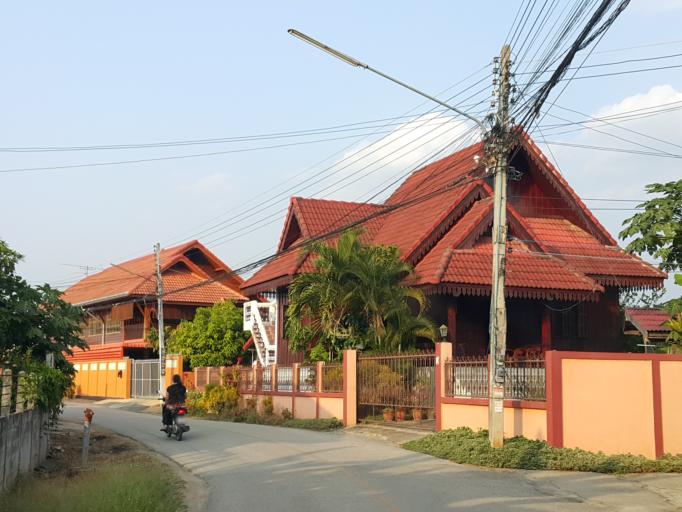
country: TH
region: Chiang Mai
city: San Sai
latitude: 18.8816
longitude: 99.1234
